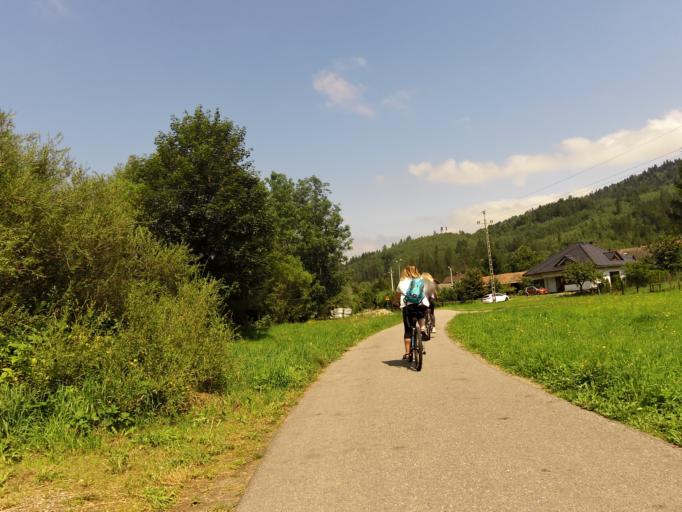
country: PL
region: Silesian Voivodeship
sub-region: Powiat zywiecki
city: Rajcza
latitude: 49.5327
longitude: 19.1083
